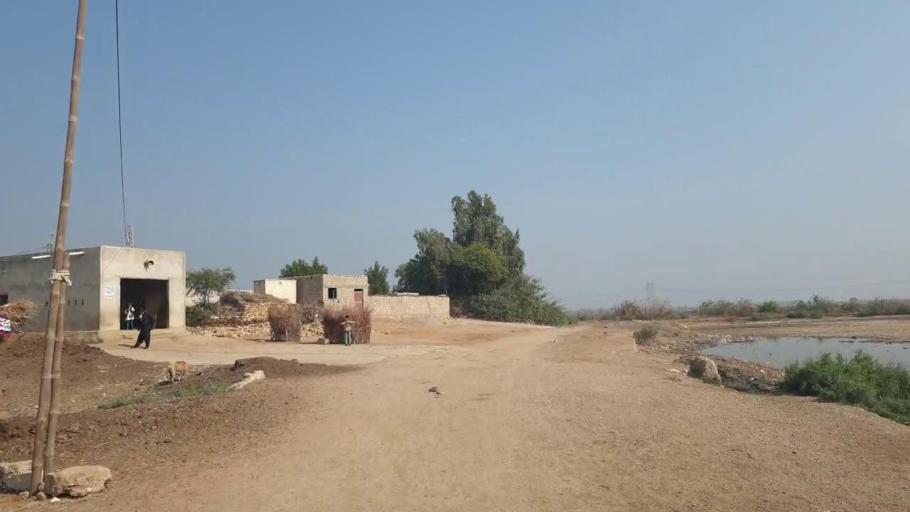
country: PK
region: Sindh
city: Jamshoro
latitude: 25.4678
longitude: 68.2891
